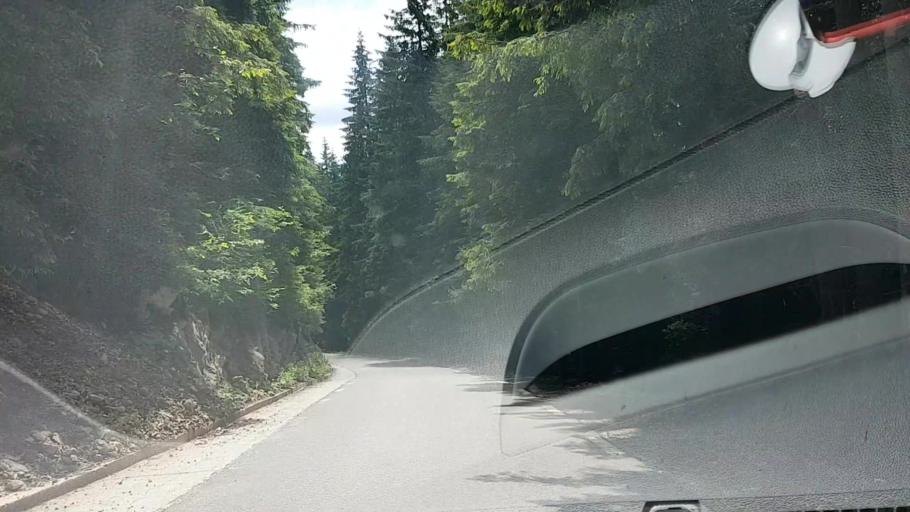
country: RO
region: Suceava
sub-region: Municipiul Campulung Moldovenesc
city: Campulung Moldovenesc
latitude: 47.4481
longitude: 25.5537
